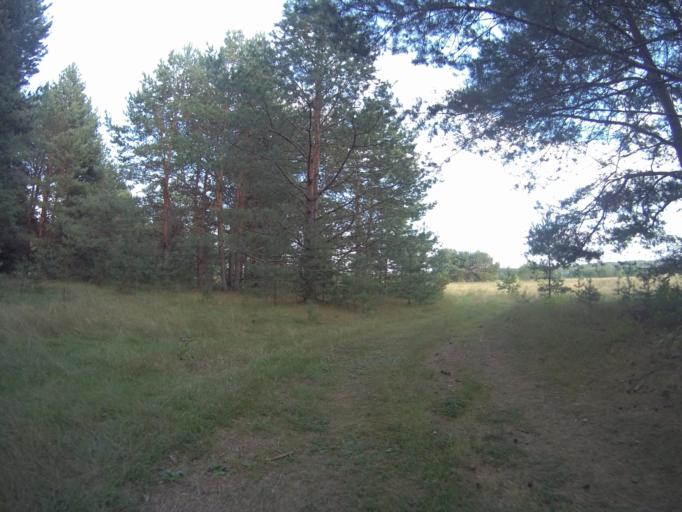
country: RU
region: Vladimir
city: Vorsha
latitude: 56.0313
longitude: 40.1708
